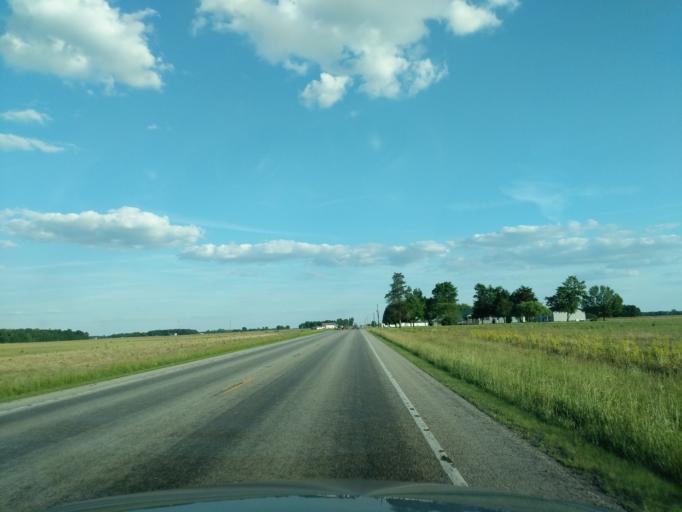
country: US
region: Indiana
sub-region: Huntington County
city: Warren
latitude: 40.7506
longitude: -85.4477
